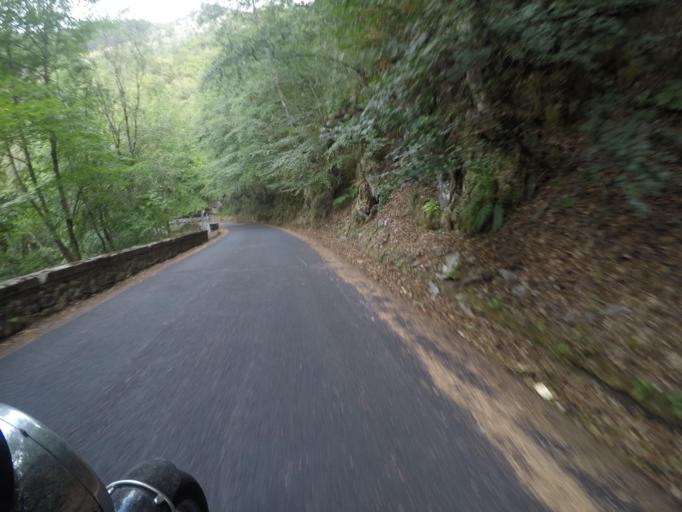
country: IT
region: Tuscany
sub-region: Provincia di Massa-Carrara
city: Carrara
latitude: 44.1202
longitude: 10.1164
